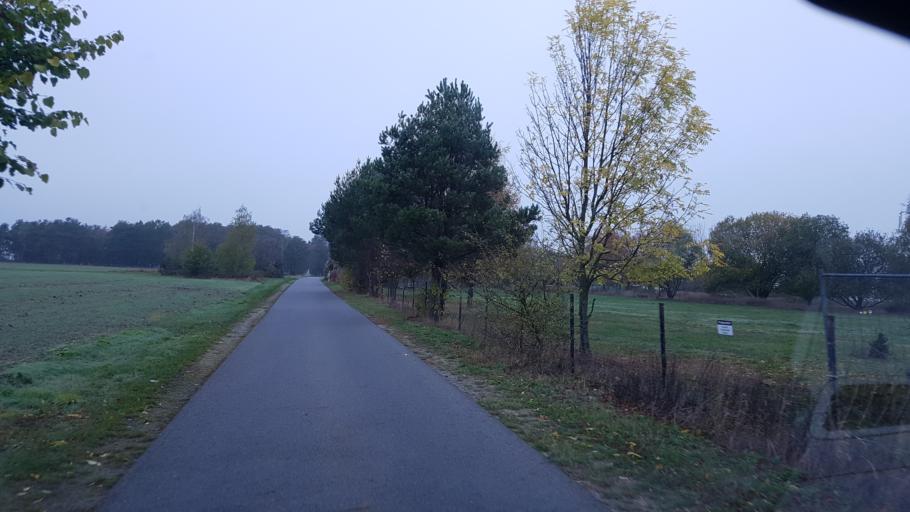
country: DE
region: Brandenburg
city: Sonnewalde
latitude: 51.6738
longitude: 13.6311
